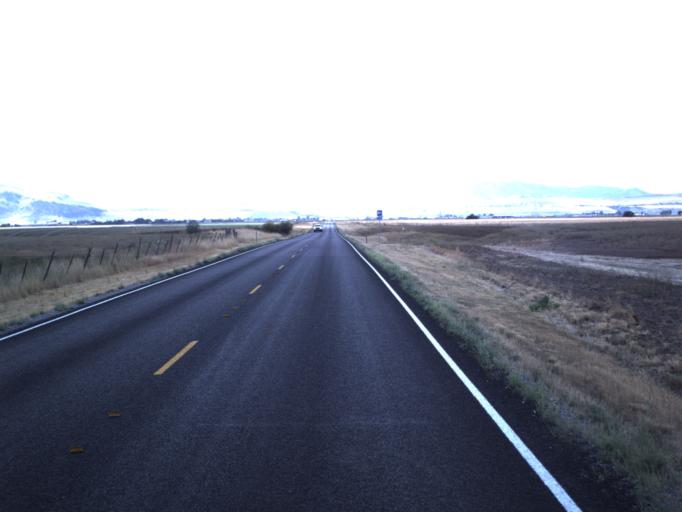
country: US
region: Utah
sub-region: Cache County
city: Richmond
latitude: 41.9250
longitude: -111.8624
